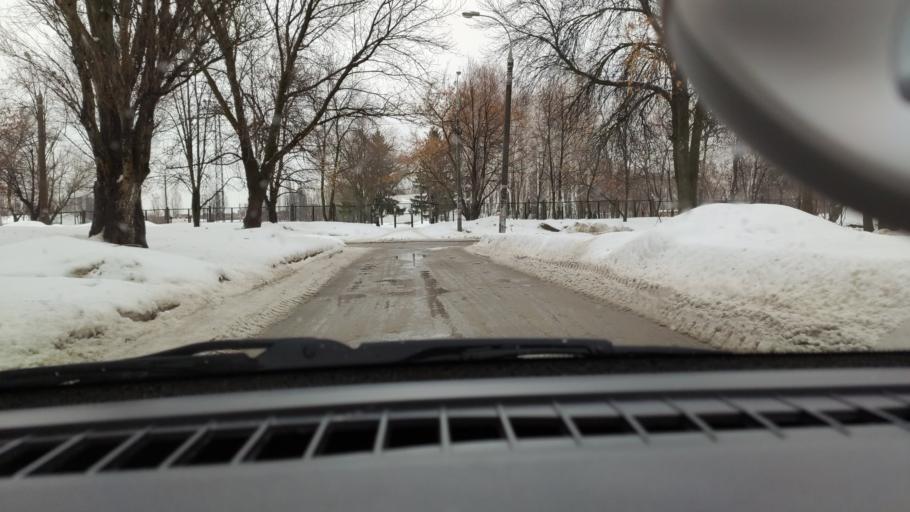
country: RU
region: Samara
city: Petra-Dubrava
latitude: 53.3037
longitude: 50.2753
